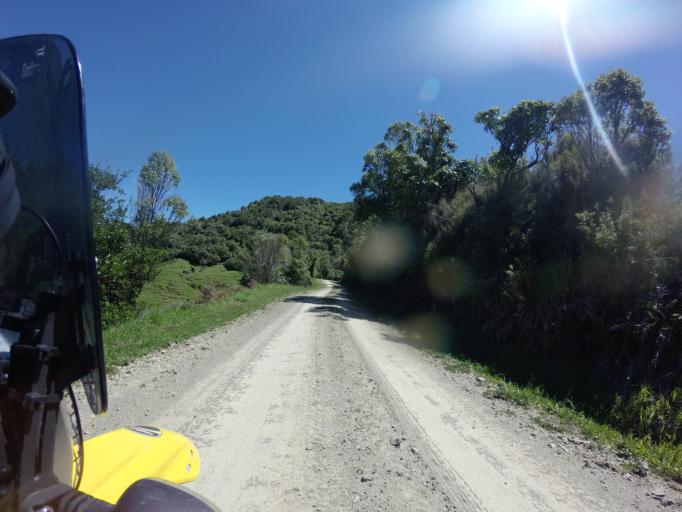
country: NZ
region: Bay of Plenty
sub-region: Opotiki District
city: Opotiki
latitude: -38.4088
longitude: 177.4401
